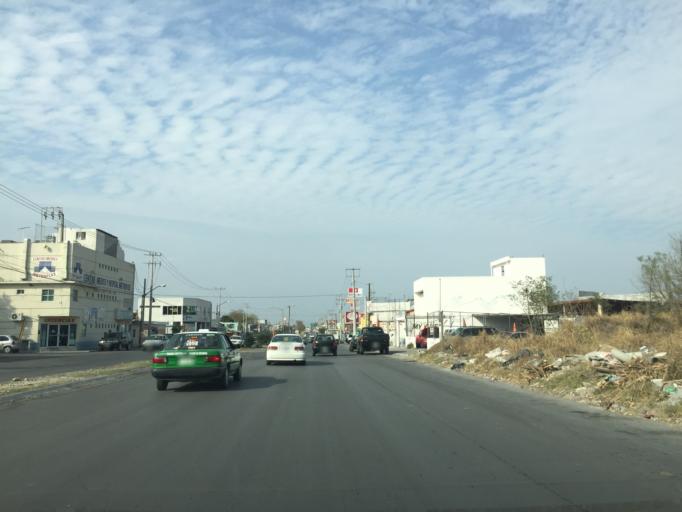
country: MX
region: Nuevo Leon
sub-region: Apodaca
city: Fraccionamiento Cosmopolis Octavo Sector
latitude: 25.7915
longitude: -100.2487
